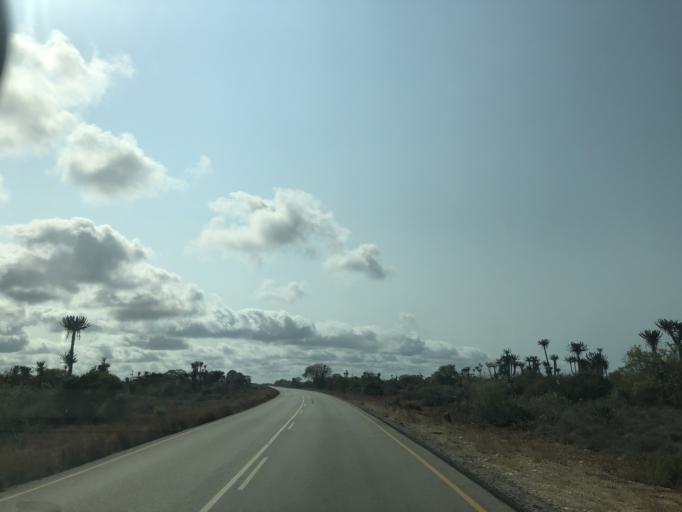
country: AO
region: Luanda
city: Luanda
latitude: -9.7079
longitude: 13.2186
